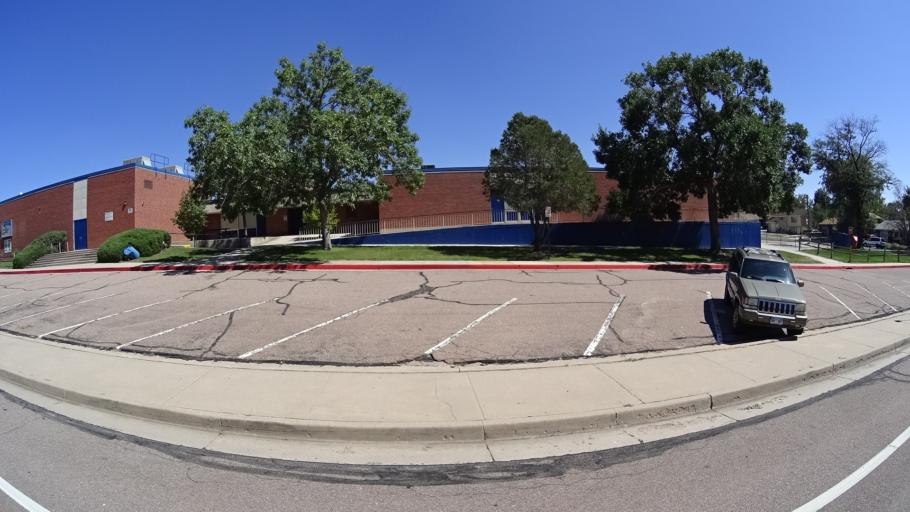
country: US
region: Colorado
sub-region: El Paso County
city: Colorado Springs
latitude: 38.8316
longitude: -104.7663
